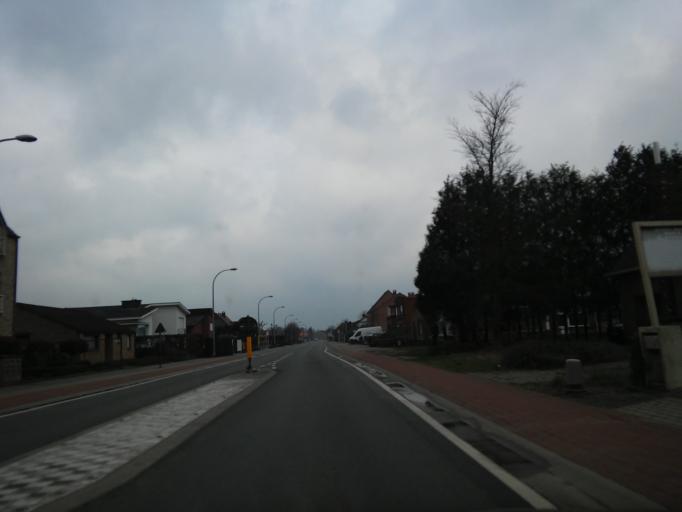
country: BE
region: Flanders
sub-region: Provincie Antwerpen
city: Herenthout
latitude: 51.1318
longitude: 4.7613
